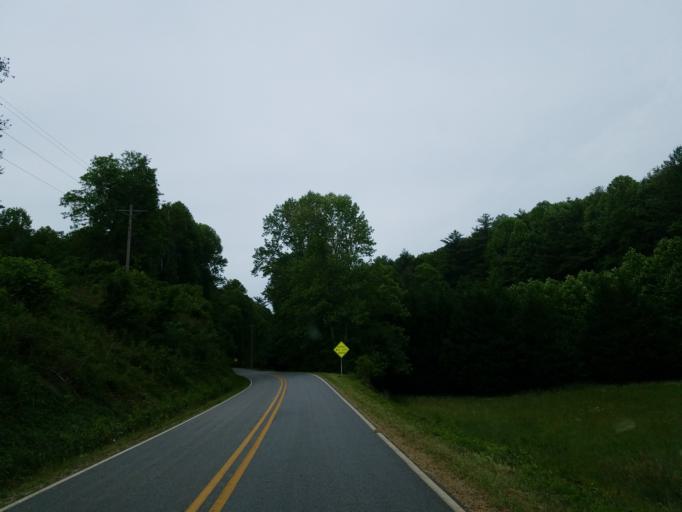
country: US
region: Georgia
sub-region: Union County
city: Blairsville
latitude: 34.7163
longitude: -83.9950
